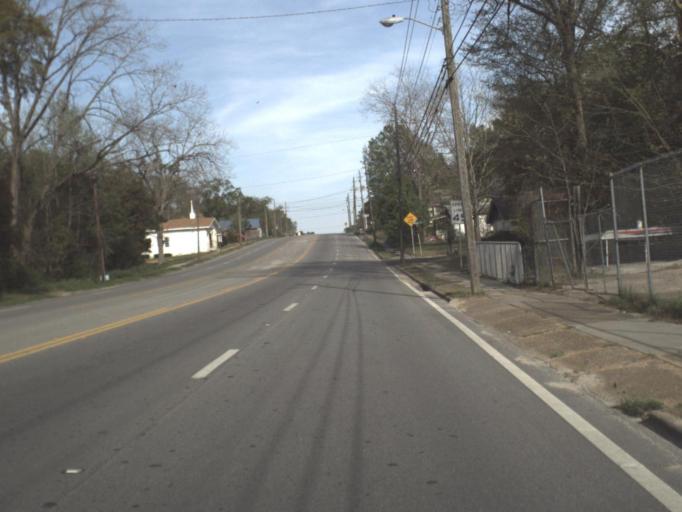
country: US
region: Florida
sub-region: Holmes County
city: Bonifay
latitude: 30.7880
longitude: -85.6782
